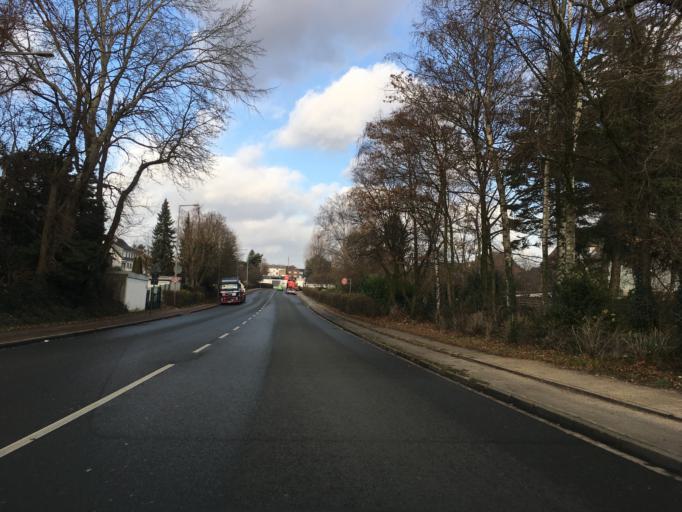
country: DE
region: North Rhine-Westphalia
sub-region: Regierungsbezirk Dusseldorf
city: Oberhausen
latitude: 51.5066
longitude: 6.8359
